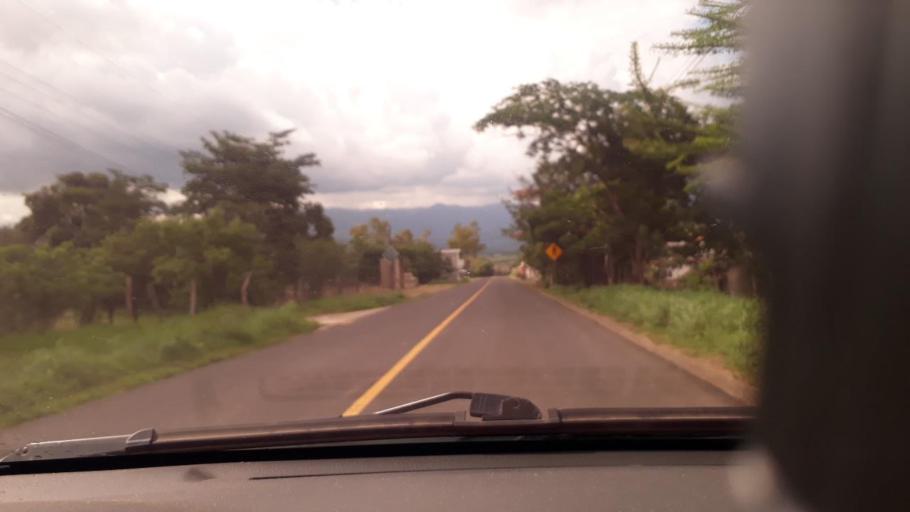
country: GT
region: Jutiapa
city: Quesada
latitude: 14.2256
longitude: -90.0254
